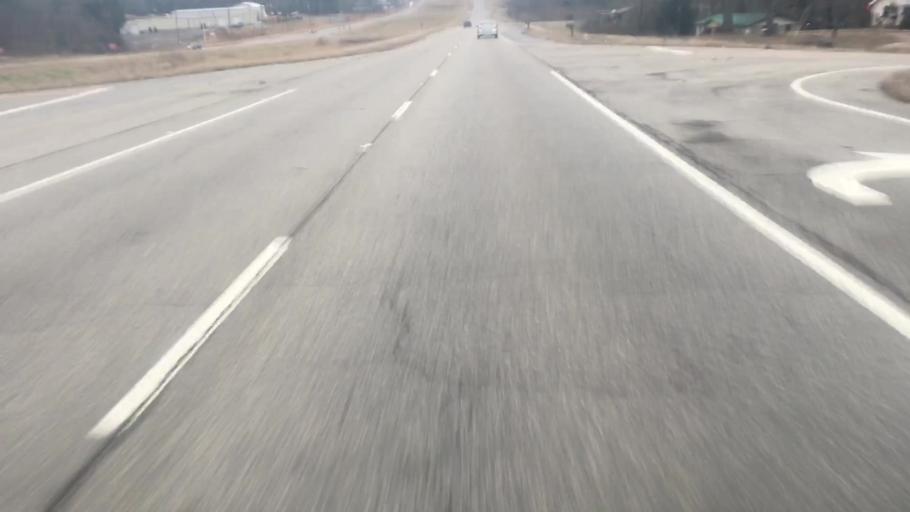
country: US
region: Alabama
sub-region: Walker County
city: Cordova
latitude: 33.8058
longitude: -87.1369
